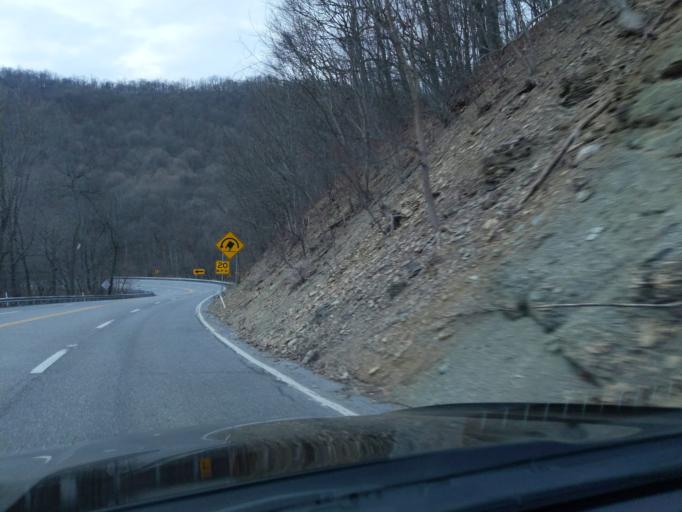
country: US
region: Pennsylvania
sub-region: Blair County
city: Williamsburg
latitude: 40.4946
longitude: -78.2422
